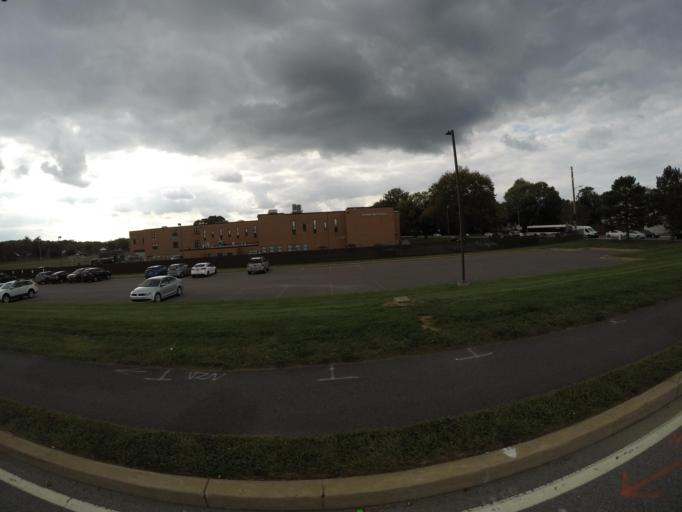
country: US
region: Delaware
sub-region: New Castle County
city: Newark
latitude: 39.6811
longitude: -75.7364
